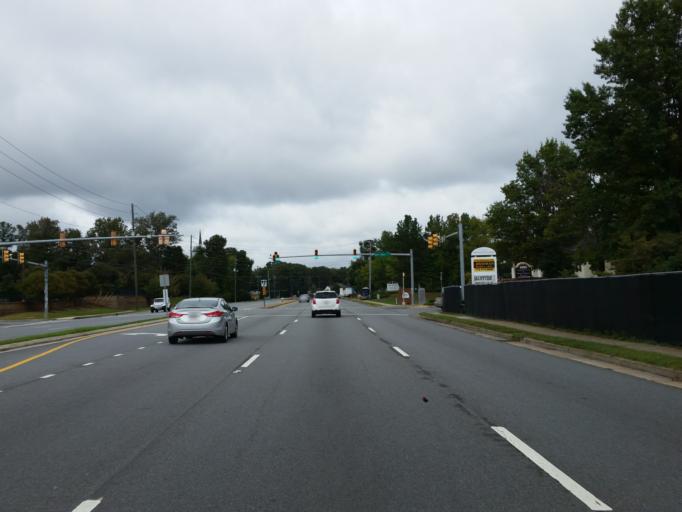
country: US
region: Georgia
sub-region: Fulton County
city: Sandy Springs
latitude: 33.9688
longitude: -84.4136
